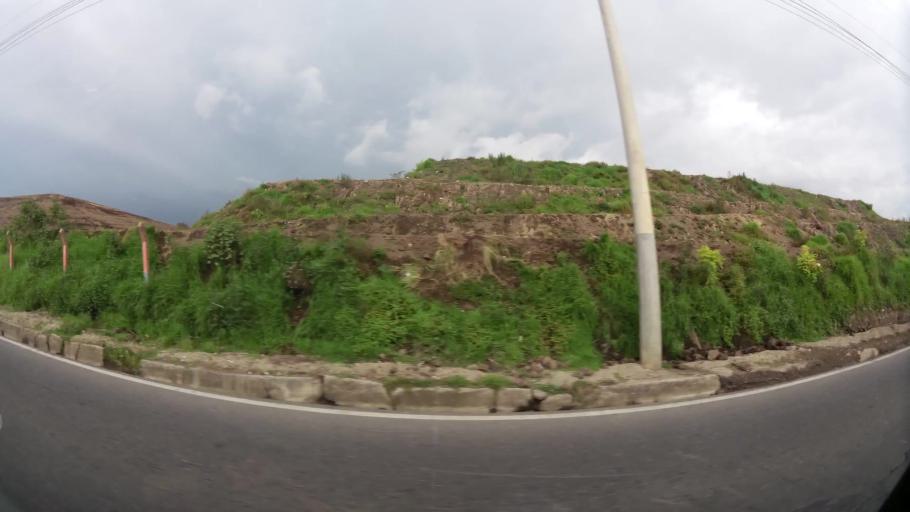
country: EC
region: Pichincha
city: Sangolqui
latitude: -0.3323
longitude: -78.5195
